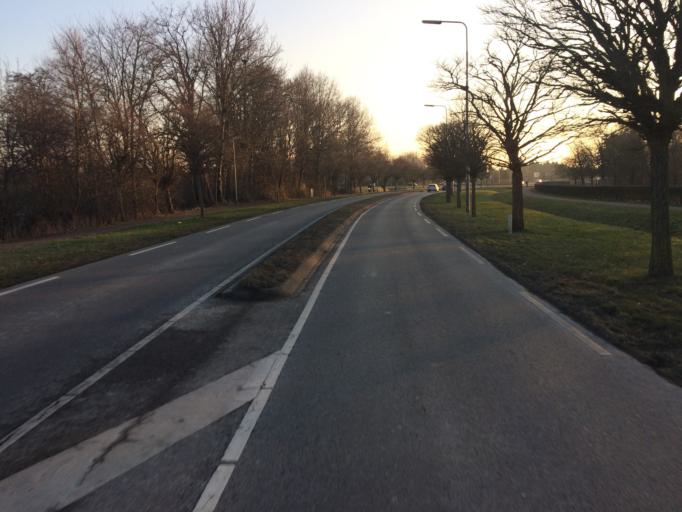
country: NL
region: Limburg
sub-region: Gemeente Maastricht
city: Heer
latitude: 50.8190
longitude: 5.7287
